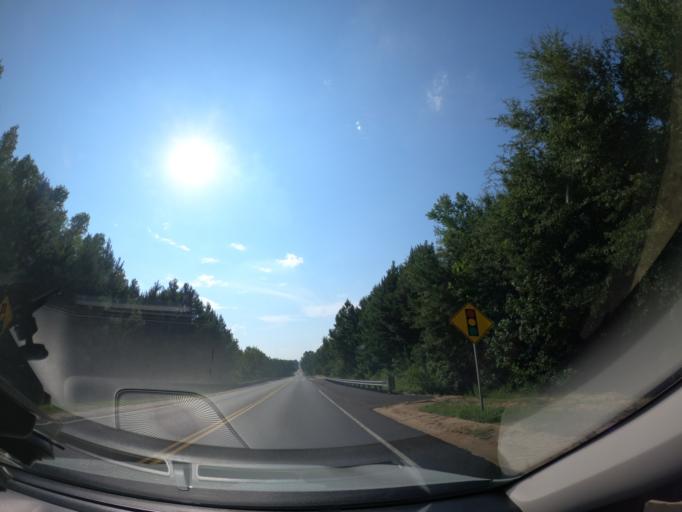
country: US
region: South Carolina
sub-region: Aiken County
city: Jackson
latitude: 33.4068
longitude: -81.7847
